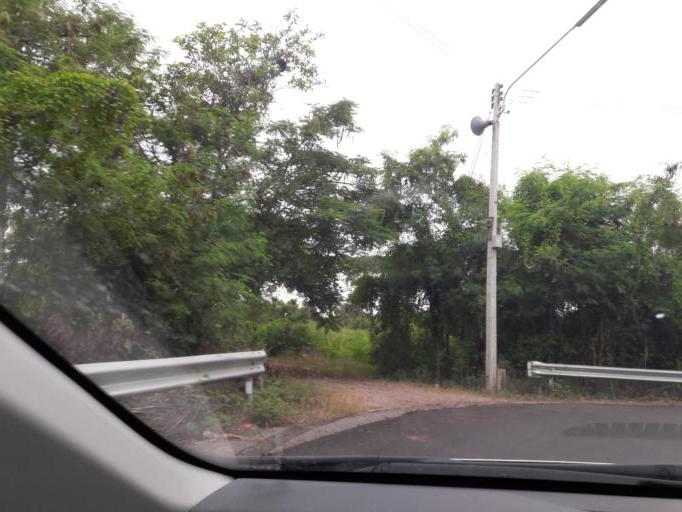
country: TH
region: Samut Sakhon
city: Ban Phaeo
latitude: 13.5968
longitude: 100.0443
